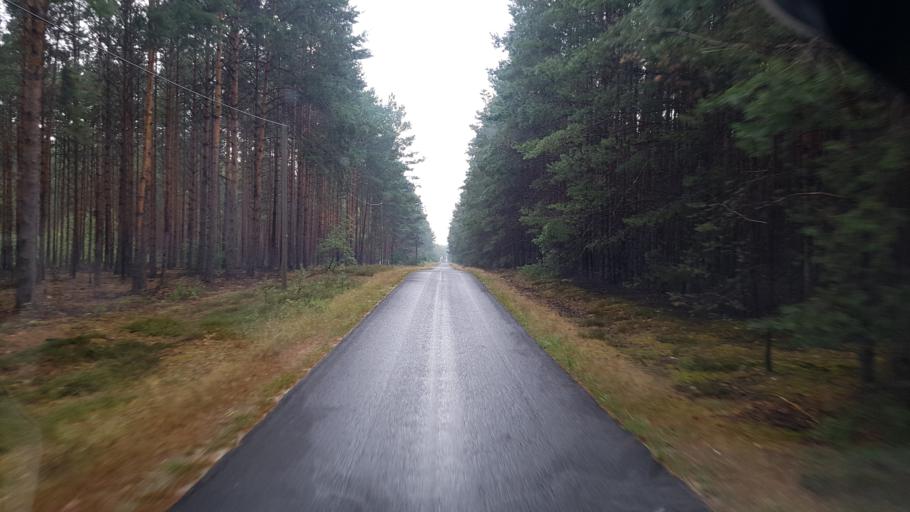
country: DE
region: Brandenburg
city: Finsterwalde
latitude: 51.6522
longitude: 13.7830
